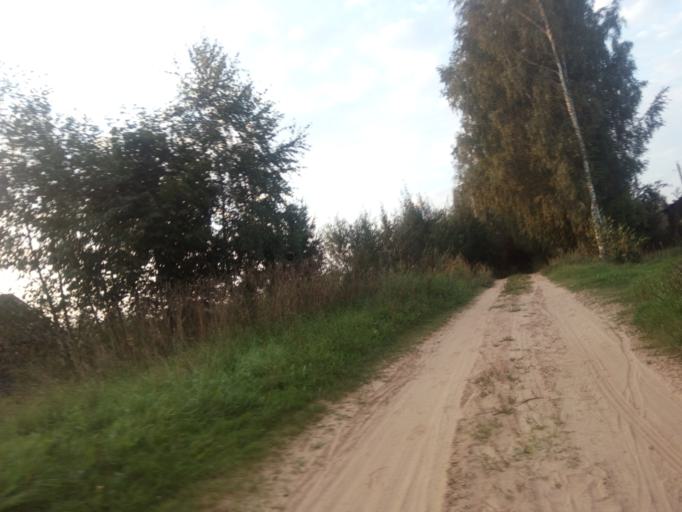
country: BY
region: Vitebsk
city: Dzisna
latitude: 55.6542
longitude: 28.3277
